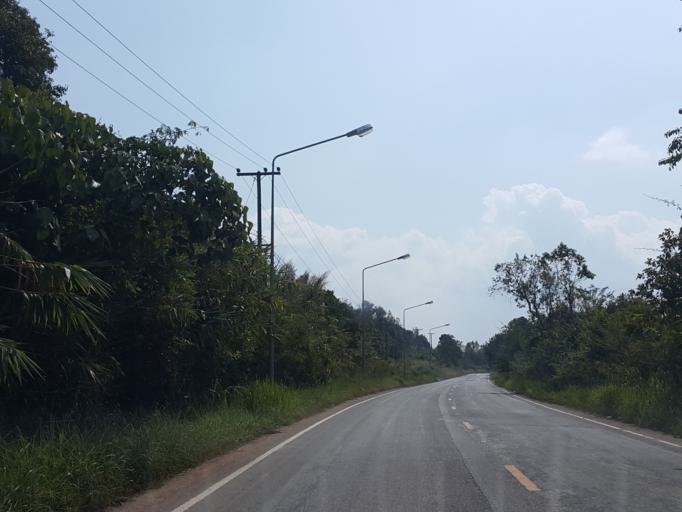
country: TH
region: Chiang Mai
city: Hot
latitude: 18.1030
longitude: 98.3752
